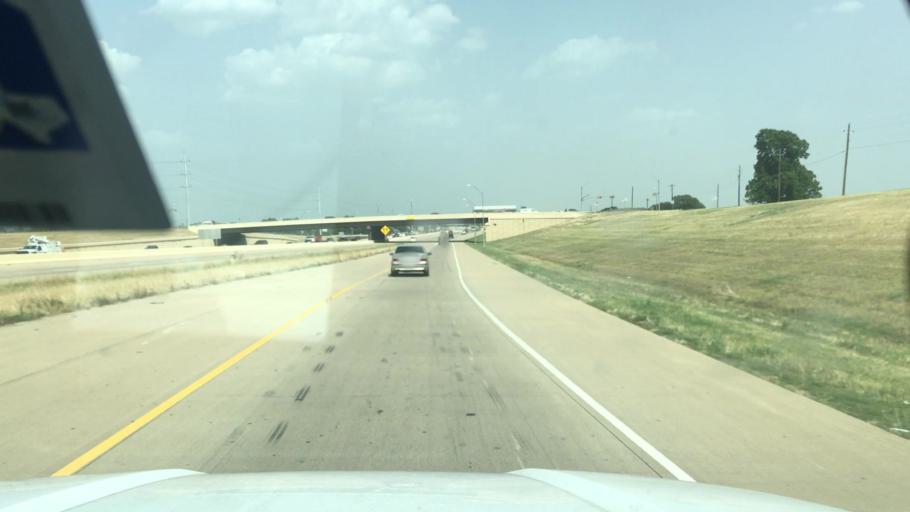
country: US
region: Texas
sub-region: Denton County
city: Roanoke
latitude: 32.9979
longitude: -97.2107
